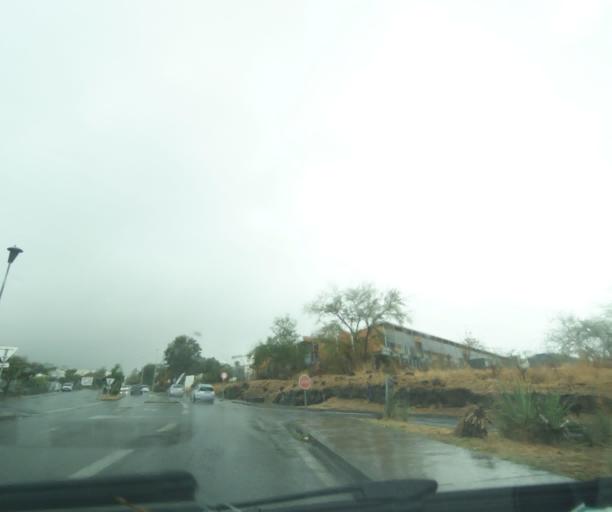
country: RE
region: Reunion
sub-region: Reunion
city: Saint-Paul
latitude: -21.0197
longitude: 55.2655
